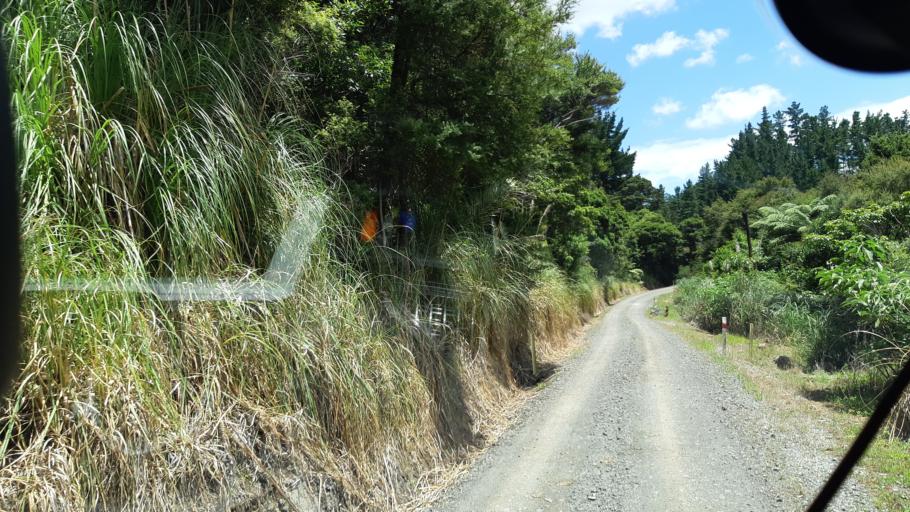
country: NZ
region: Northland
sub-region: Far North District
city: Kaitaia
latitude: -35.2225
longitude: 173.3118
